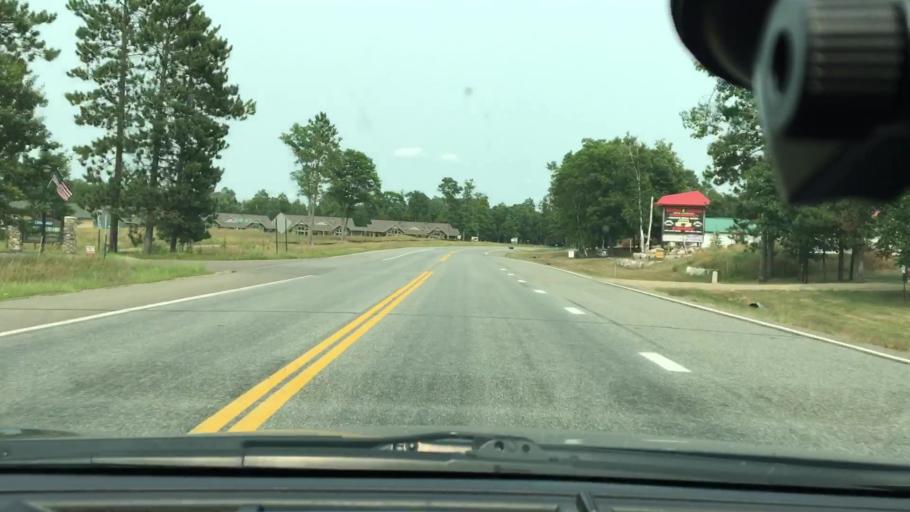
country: US
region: Minnesota
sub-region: Crow Wing County
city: Cross Lake
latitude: 46.6695
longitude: -94.1019
